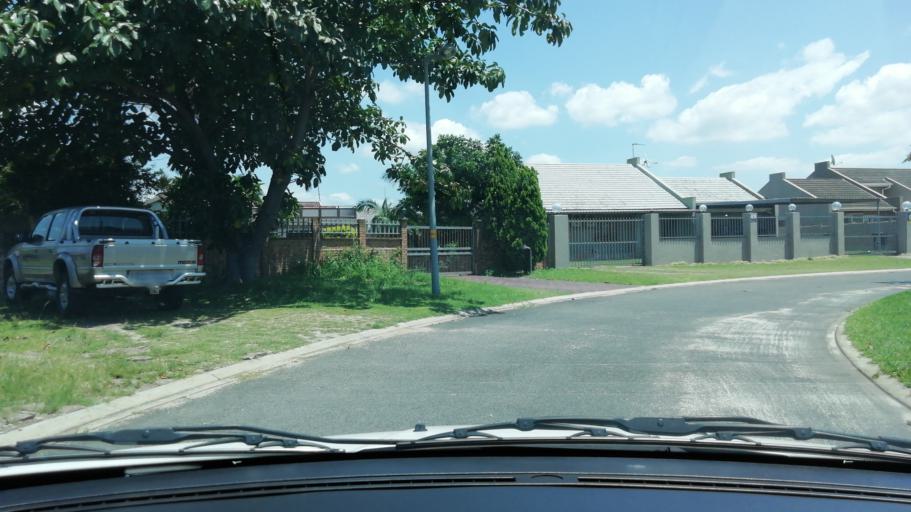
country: ZA
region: KwaZulu-Natal
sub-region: uThungulu District Municipality
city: Richards Bay
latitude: -28.7370
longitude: 32.0462
